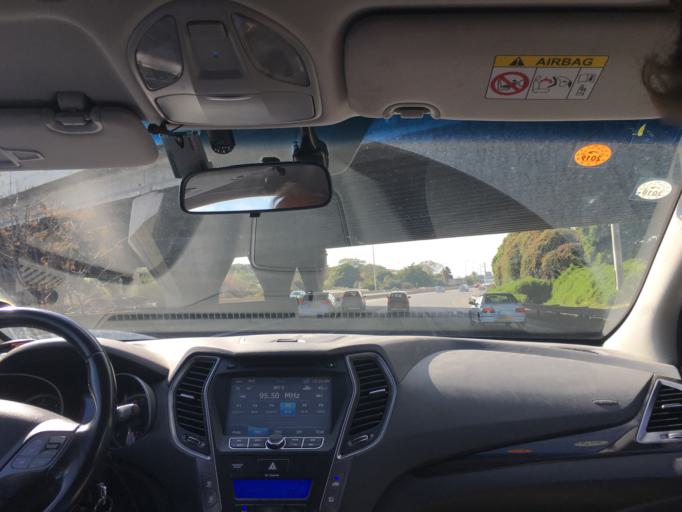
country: IL
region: Tel Aviv
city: Bene Beraq
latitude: 32.0560
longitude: 34.8349
